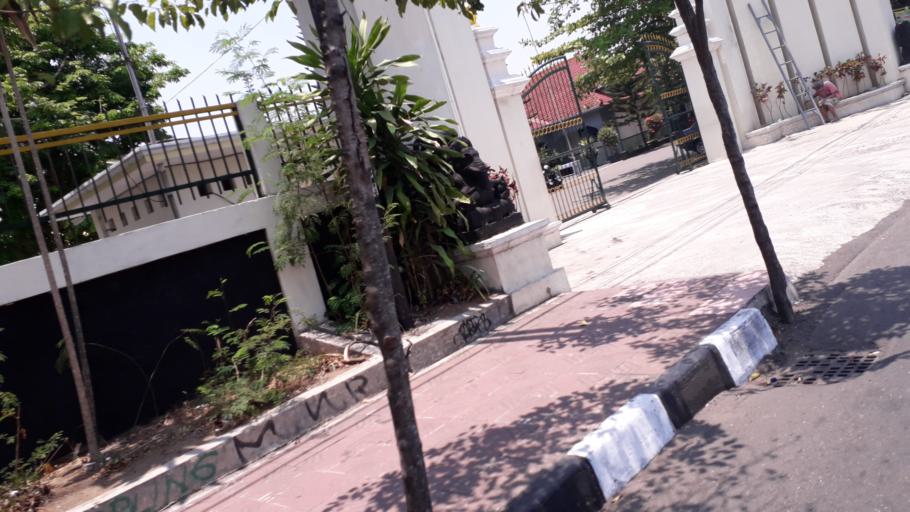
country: ID
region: Daerah Istimewa Yogyakarta
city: Yogyakarta
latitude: -7.7770
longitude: 110.3678
